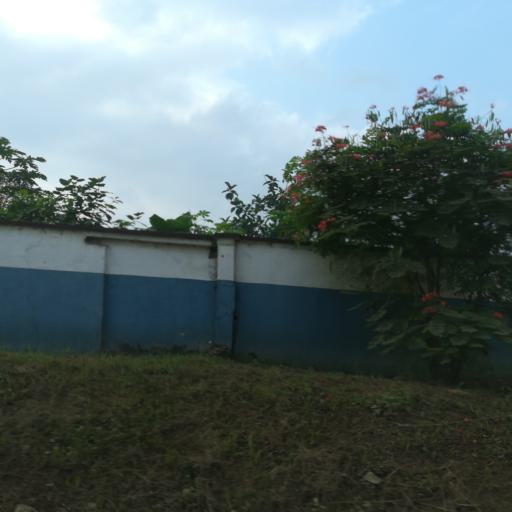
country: NG
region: Rivers
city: Okrika
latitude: 4.7838
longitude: 7.1328
